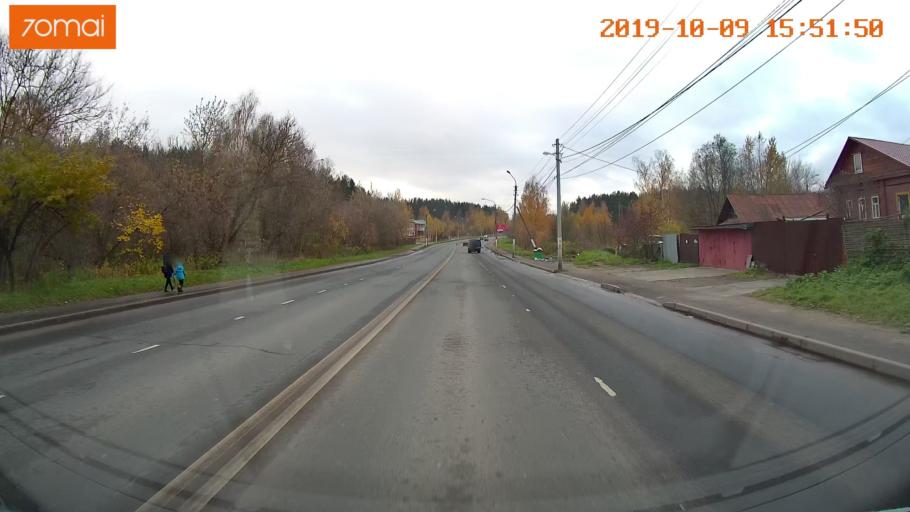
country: RU
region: Kostroma
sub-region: Kostromskoy Rayon
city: Kostroma
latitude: 57.7943
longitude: 40.9752
